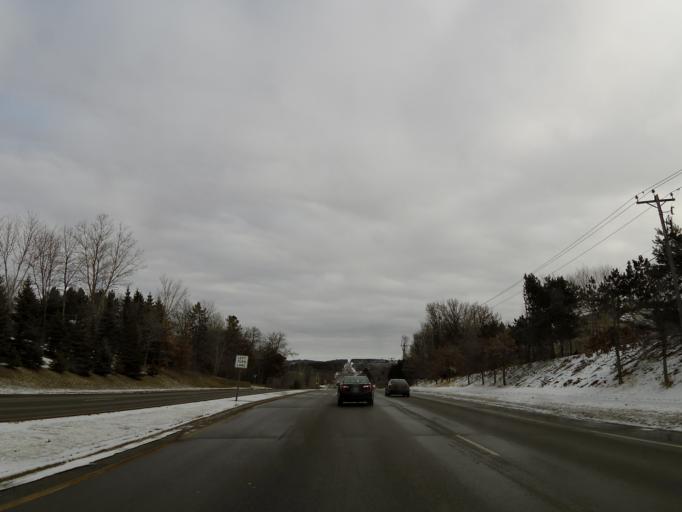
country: US
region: Minnesota
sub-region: Washington County
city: Woodbury
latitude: 44.9198
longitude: -92.9154
